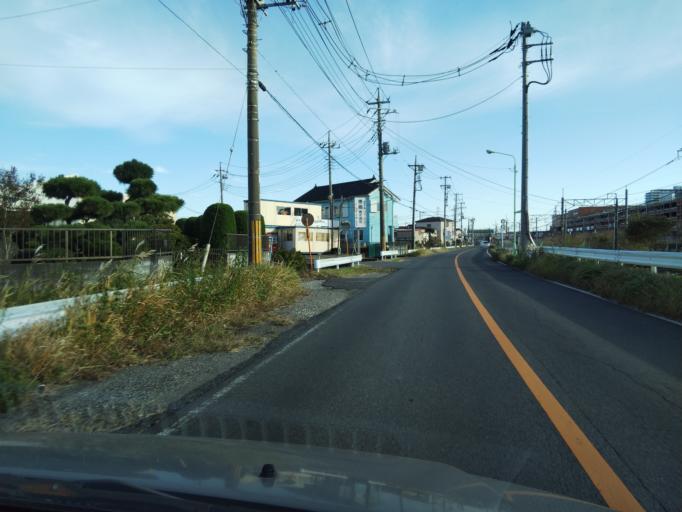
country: JP
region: Saitama
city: Yoshikawa
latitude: 35.8631
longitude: 139.8646
